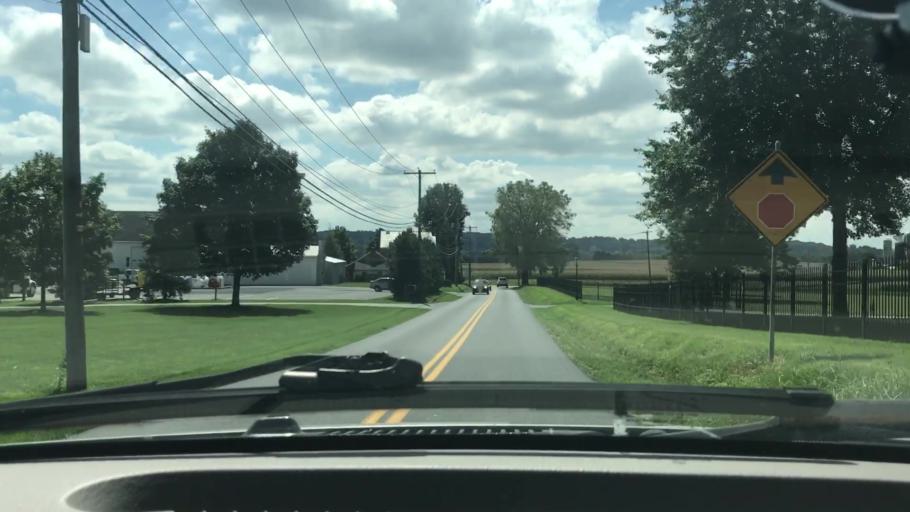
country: US
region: Pennsylvania
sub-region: Lancaster County
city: Landisville
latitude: 40.1039
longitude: -76.3870
